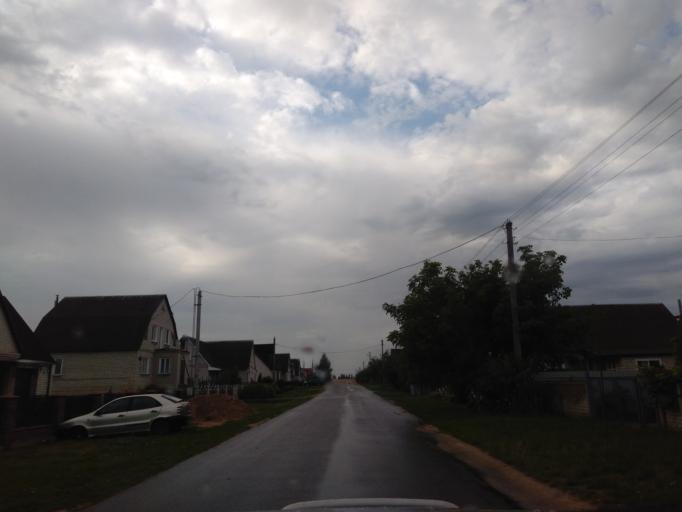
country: BY
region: Minsk
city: Kapyl'
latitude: 53.1647
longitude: 27.0814
